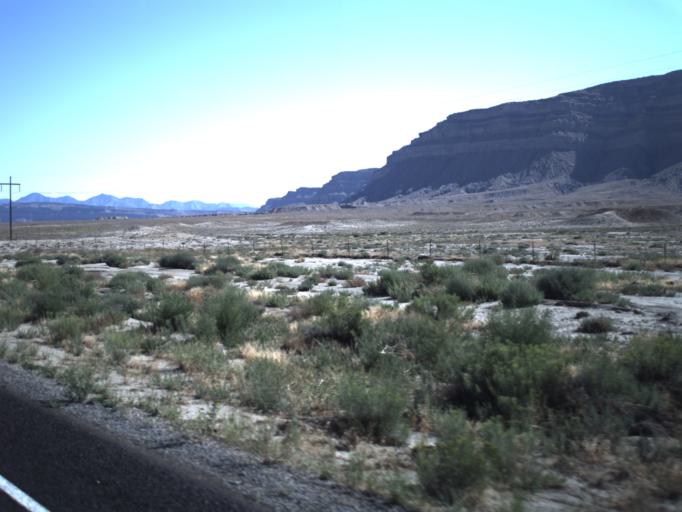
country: US
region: Utah
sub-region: Carbon County
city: East Carbon City
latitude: 39.1708
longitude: -110.3382
